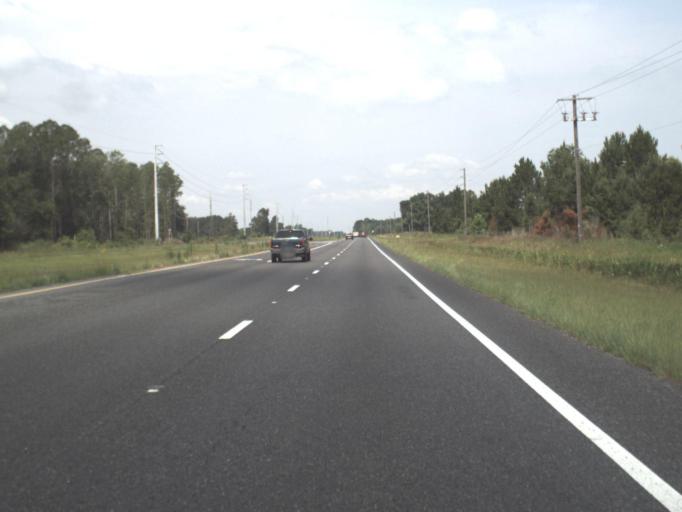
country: US
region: Florida
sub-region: Levy County
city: Bronson
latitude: 29.4760
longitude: -82.7245
